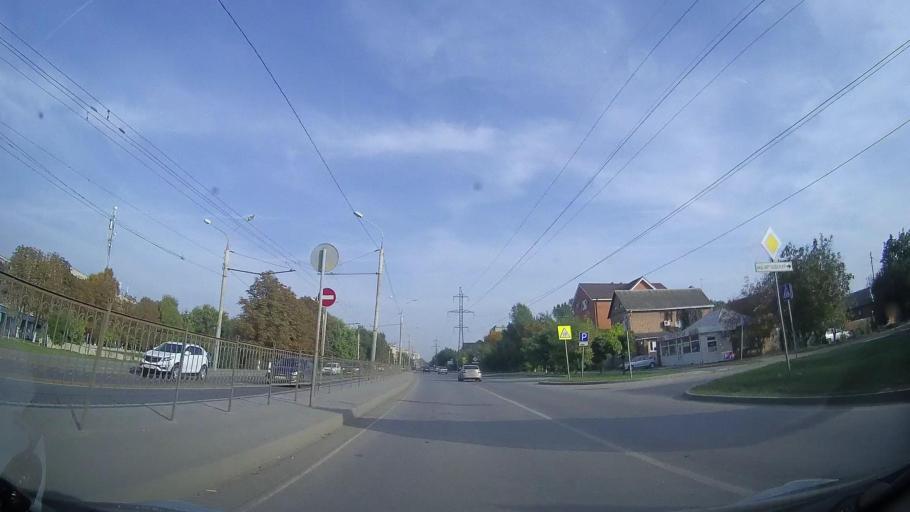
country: RU
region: Rostov
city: Imeni Chkalova
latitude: 47.2856
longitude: 39.7454
